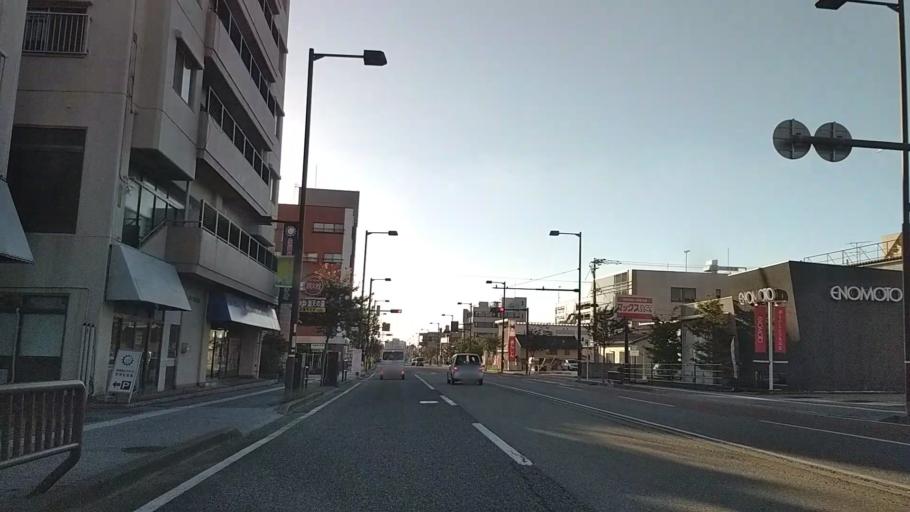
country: JP
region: Ishikawa
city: Nonoichi
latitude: 36.5581
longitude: 136.6450
